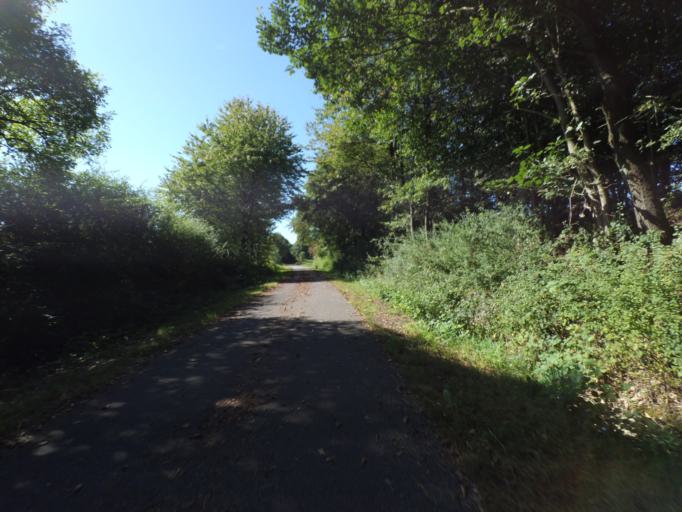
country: DE
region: Rheinland-Pfalz
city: Wallscheid
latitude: 50.1152
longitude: 6.8743
